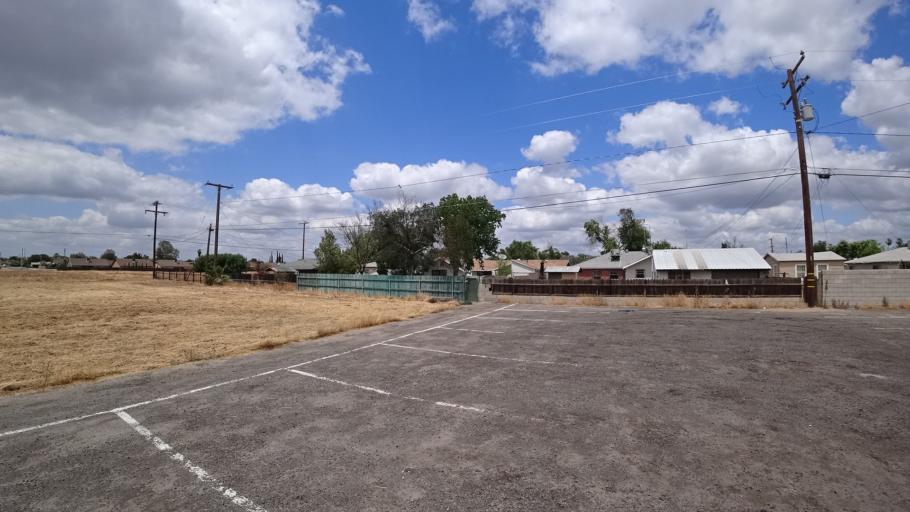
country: US
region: California
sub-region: Kings County
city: Hanford
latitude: 36.3154
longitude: -119.6582
